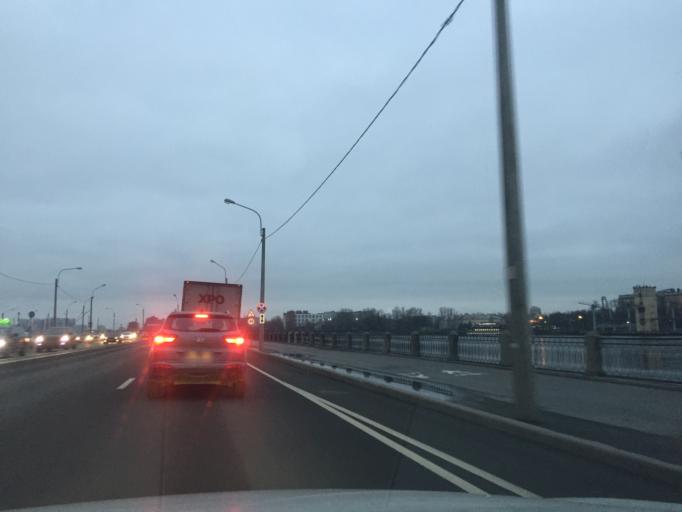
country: RU
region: St.-Petersburg
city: Centralniy
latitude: 59.9142
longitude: 30.4156
